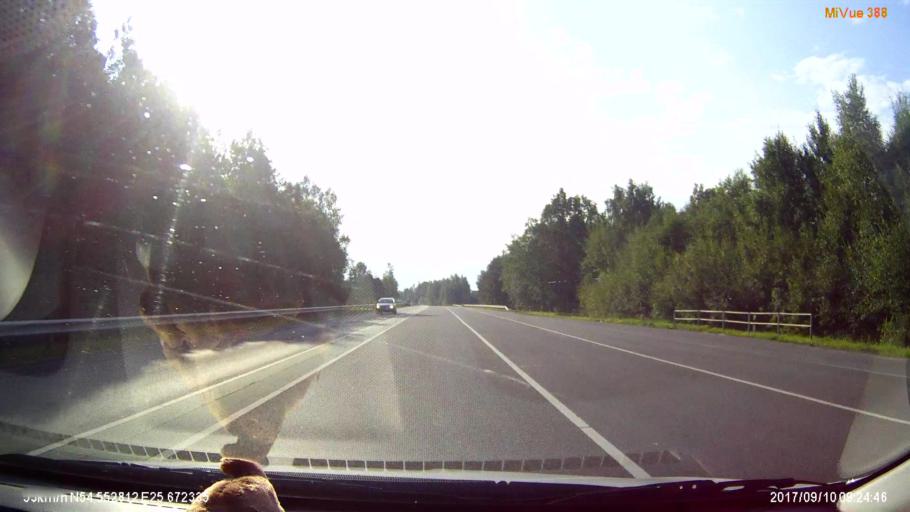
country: BY
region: Grodnenskaya
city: Astravyets
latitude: 54.5526
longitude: 25.6726
